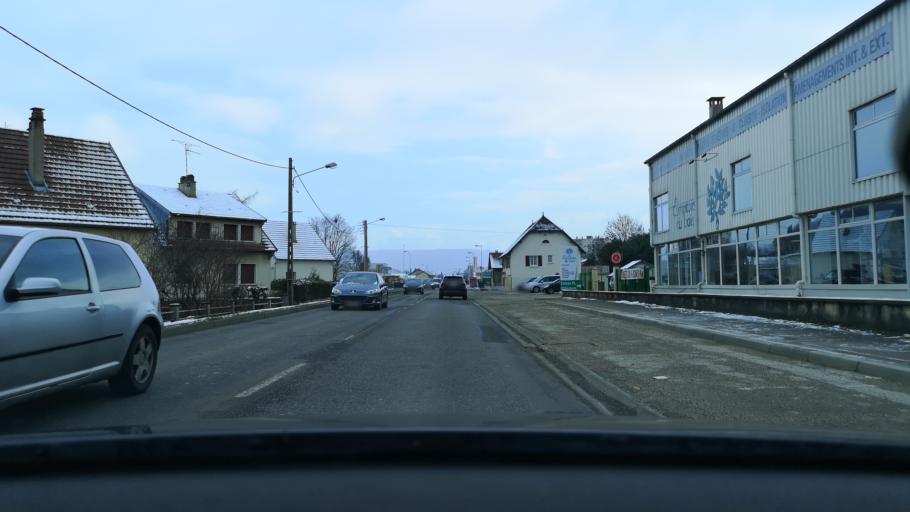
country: FR
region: Franche-Comte
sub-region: Departement du Jura
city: Montmorot
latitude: 46.6768
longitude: 5.5210
